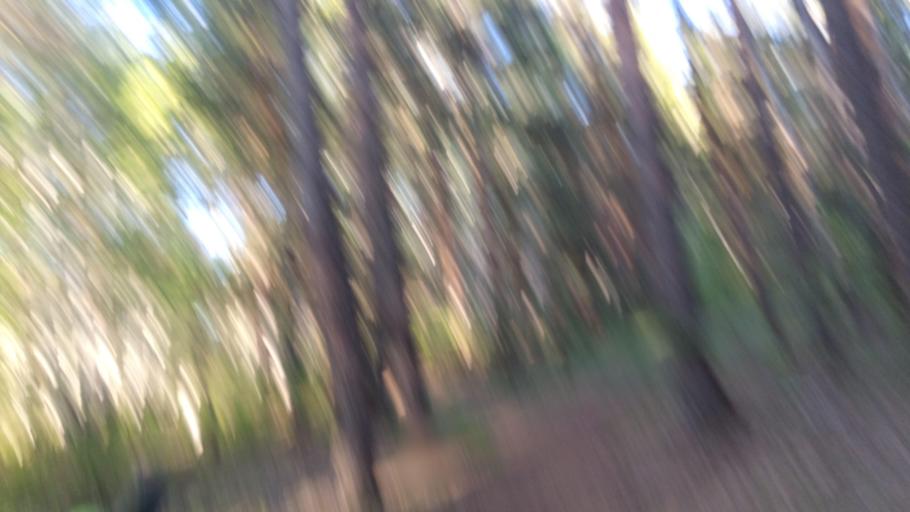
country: RU
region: Chelyabinsk
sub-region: Gorod Chelyabinsk
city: Chelyabinsk
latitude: 55.1513
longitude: 61.3333
